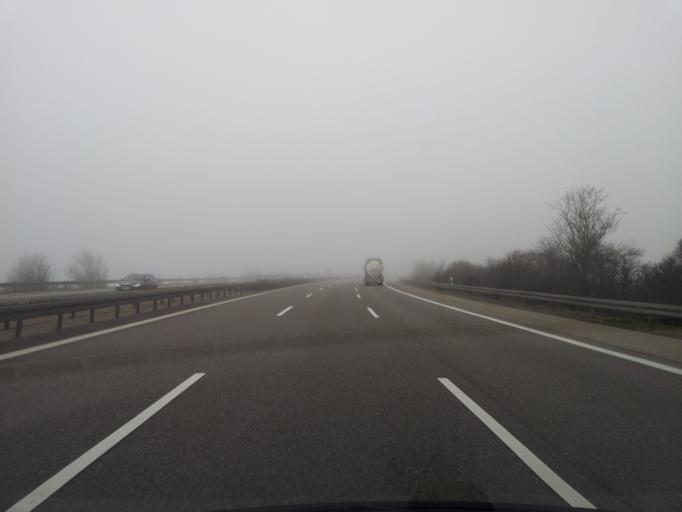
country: DE
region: Baden-Wuerttemberg
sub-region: Freiburg Region
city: Engen
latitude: 47.8890
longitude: 8.7473
